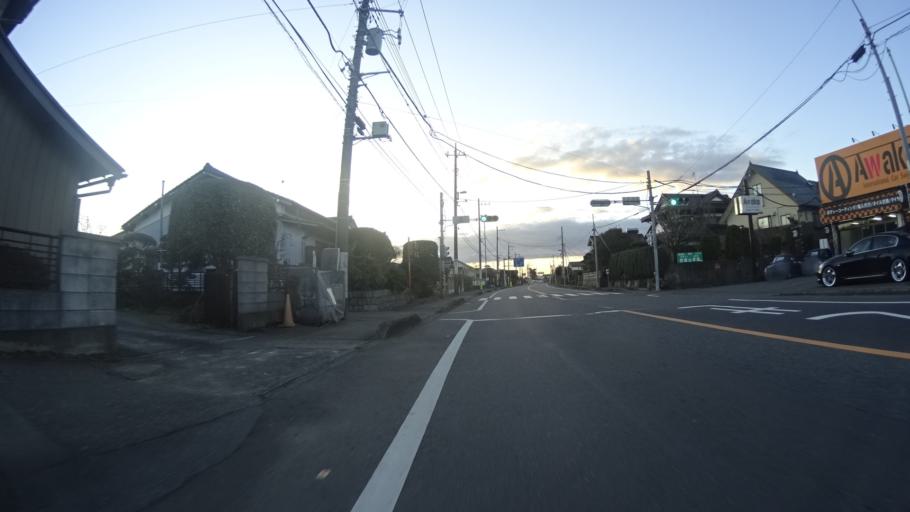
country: JP
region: Kanagawa
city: Zama
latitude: 35.5254
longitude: 139.3651
